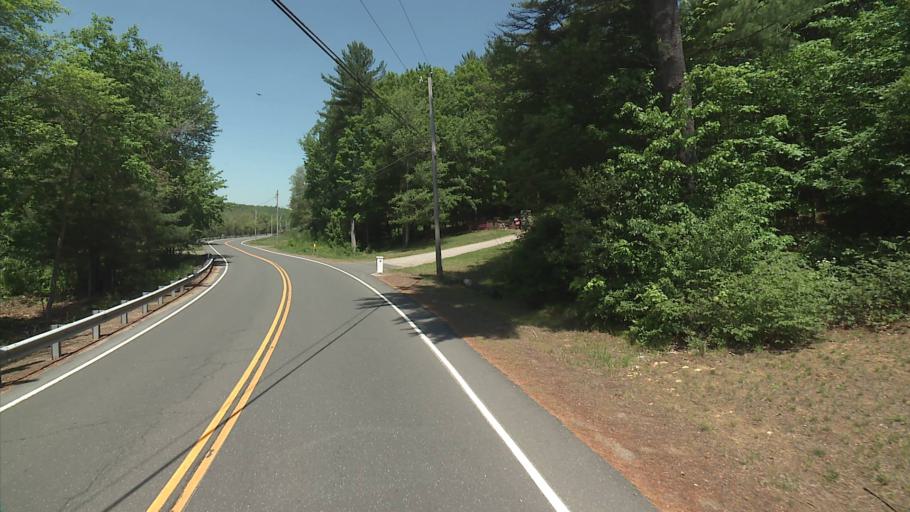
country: US
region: Connecticut
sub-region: Tolland County
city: Stafford
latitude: 42.0003
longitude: -72.2548
